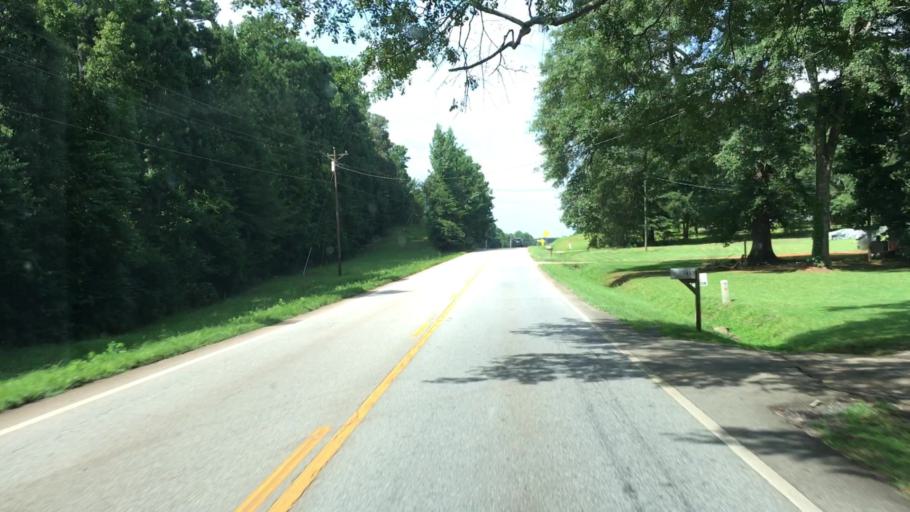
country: US
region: Georgia
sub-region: Monroe County
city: Forsyth
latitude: 33.0689
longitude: -83.9186
